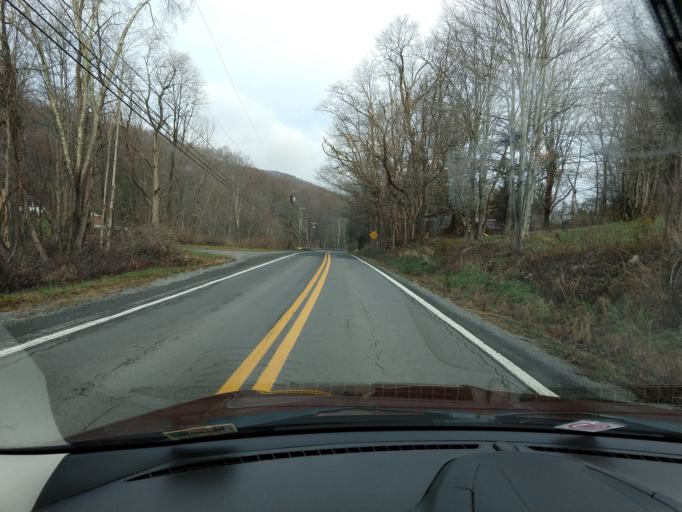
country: US
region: West Virginia
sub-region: Greenbrier County
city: Rainelle
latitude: 38.0627
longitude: -80.7079
